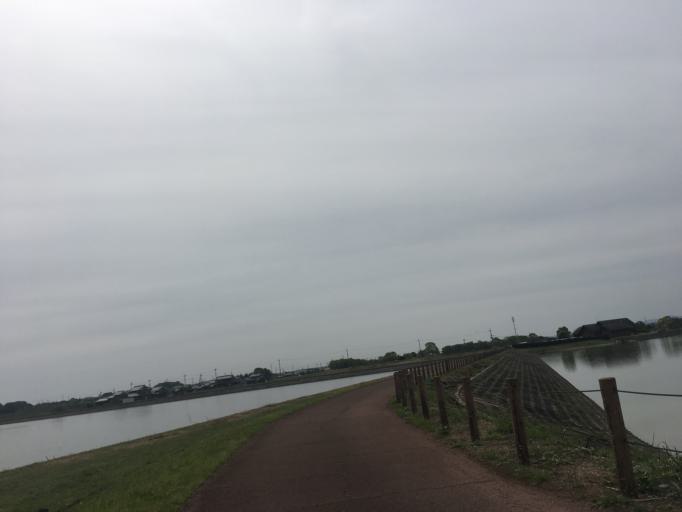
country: JP
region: Hyogo
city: Miki
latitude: 34.7695
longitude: 134.9245
